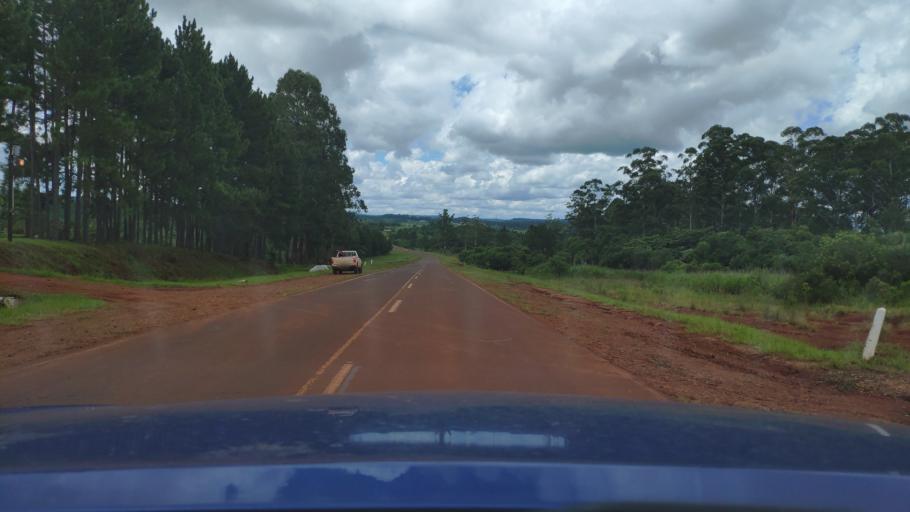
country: AR
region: Misiones
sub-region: Departamento de San Javier
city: San Javier
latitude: -27.8541
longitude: -55.2492
